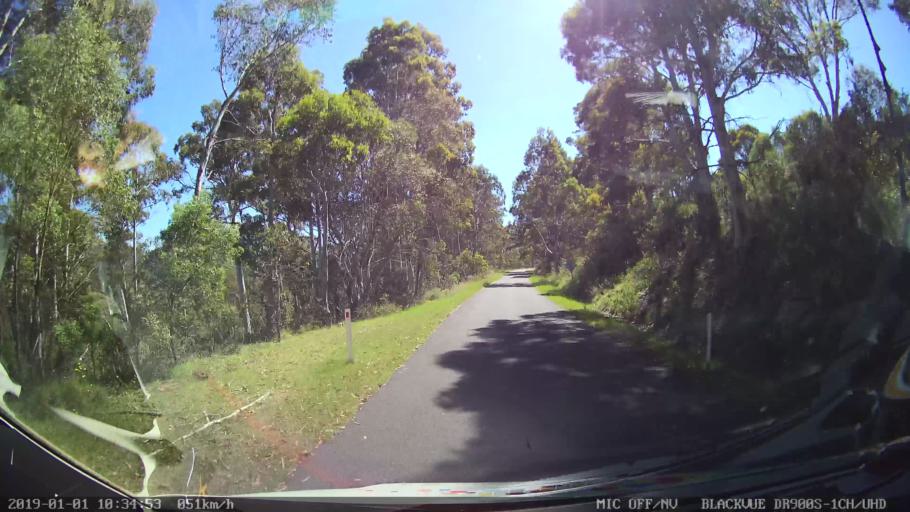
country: AU
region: New South Wales
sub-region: Snowy River
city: Jindabyne
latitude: -36.0475
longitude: 148.2851
